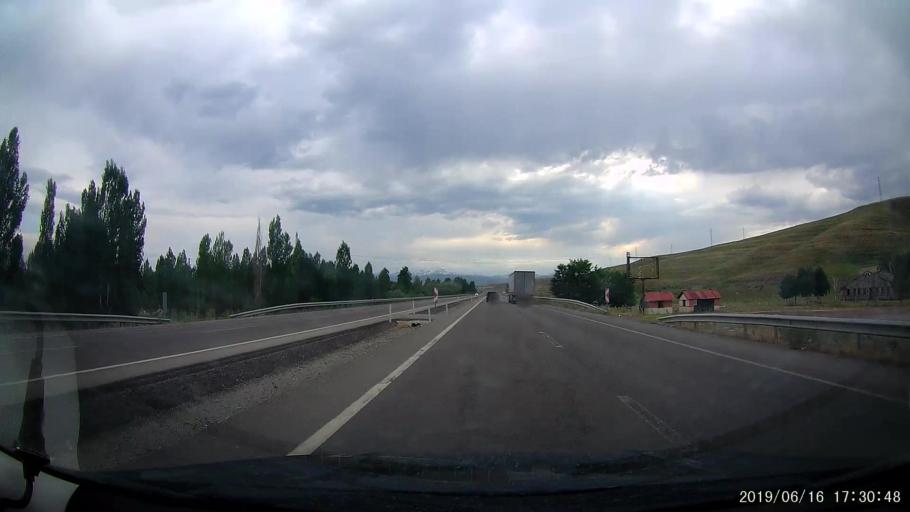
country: TR
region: Erzincan
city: Tercan
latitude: 39.7754
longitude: 40.3385
